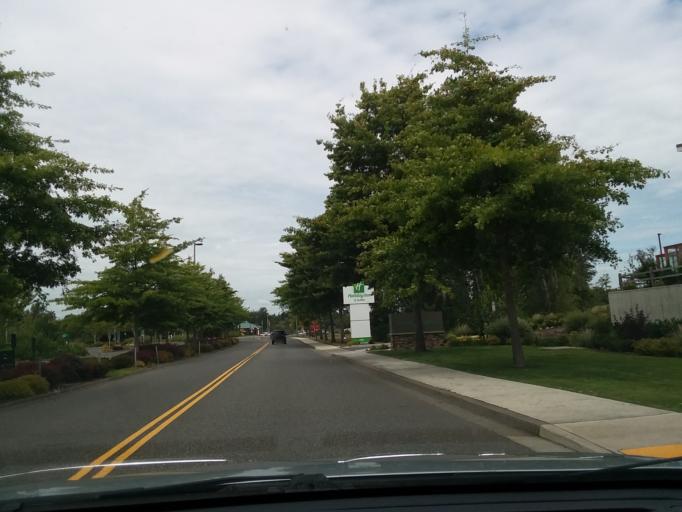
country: US
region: Washington
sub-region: Whatcom County
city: Marietta-Alderwood
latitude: 48.7963
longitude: -122.5306
